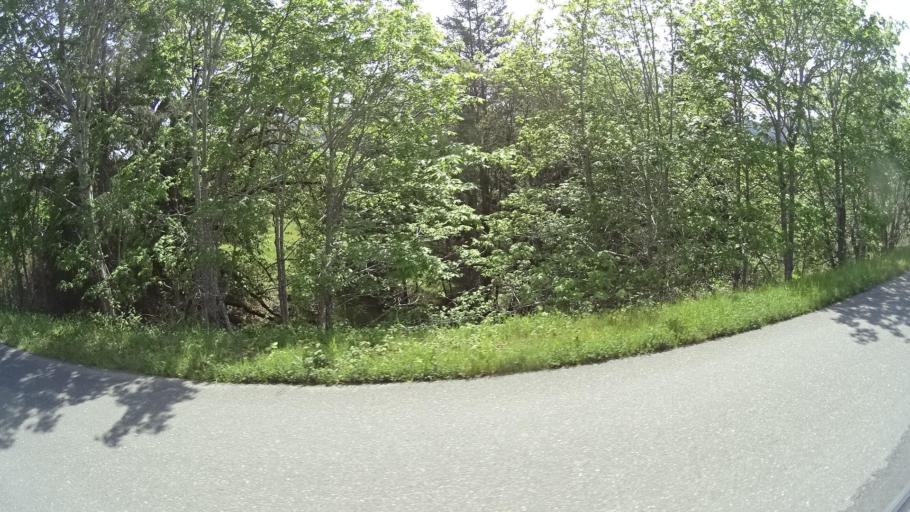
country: US
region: California
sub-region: Humboldt County
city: Redway
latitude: 40.4134
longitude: -123.7580
